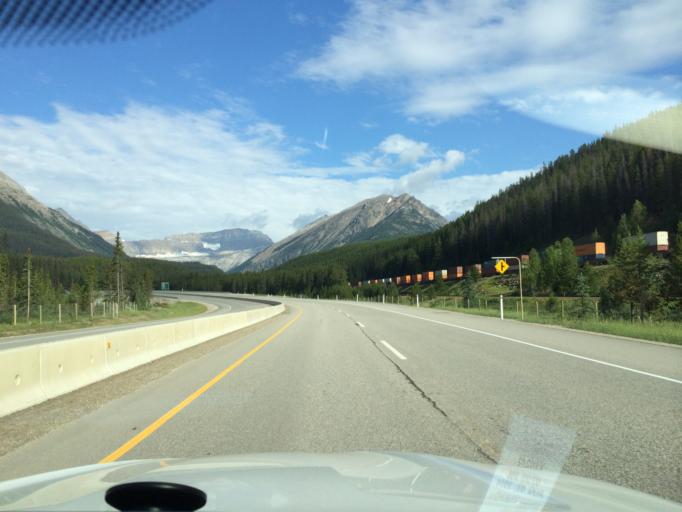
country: CA
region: Alberta
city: Lake Louise
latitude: 51.4566
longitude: -116.2626
